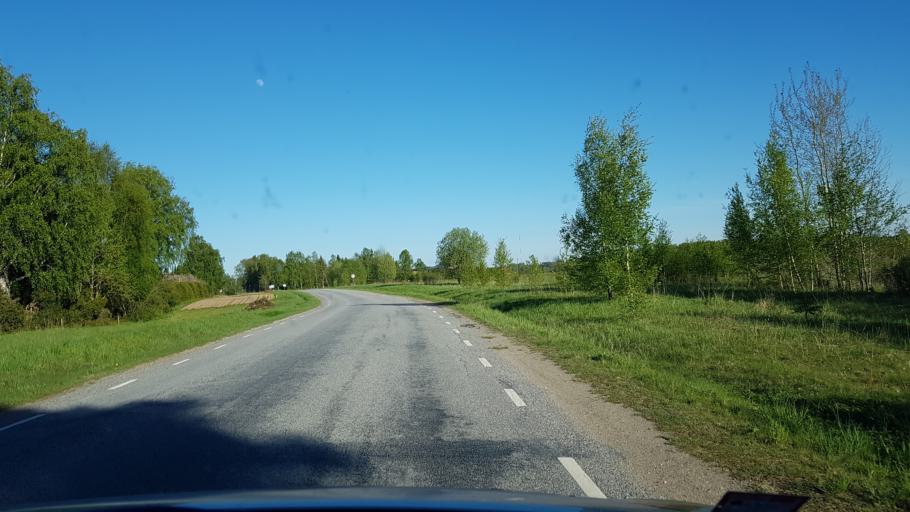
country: EE
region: Vorumaa
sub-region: Voru linn
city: Voru
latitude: 57.9068
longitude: 26.9785
